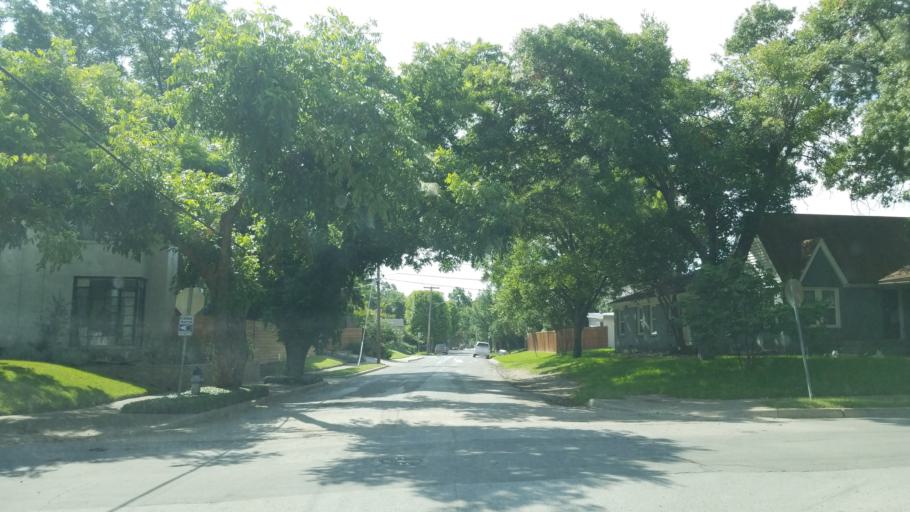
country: US
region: Texas
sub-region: Dallas County
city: Highland Park
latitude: 32.8186
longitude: -96.7864
